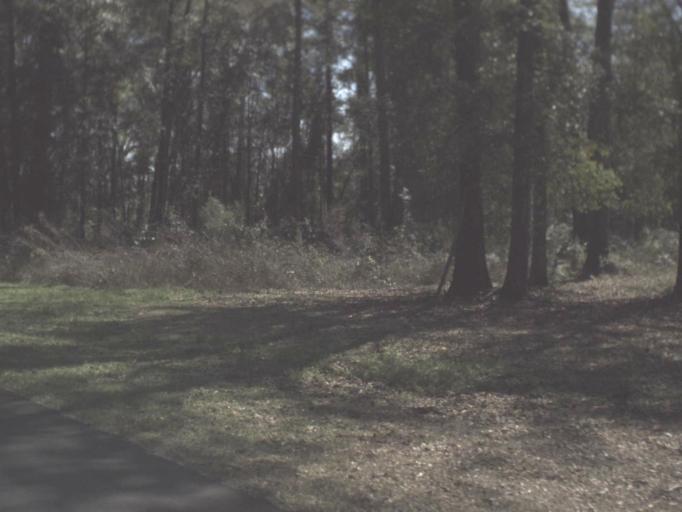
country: US
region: Florida
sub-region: Jackson County
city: Malone
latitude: 30.8591
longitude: -85.0988
